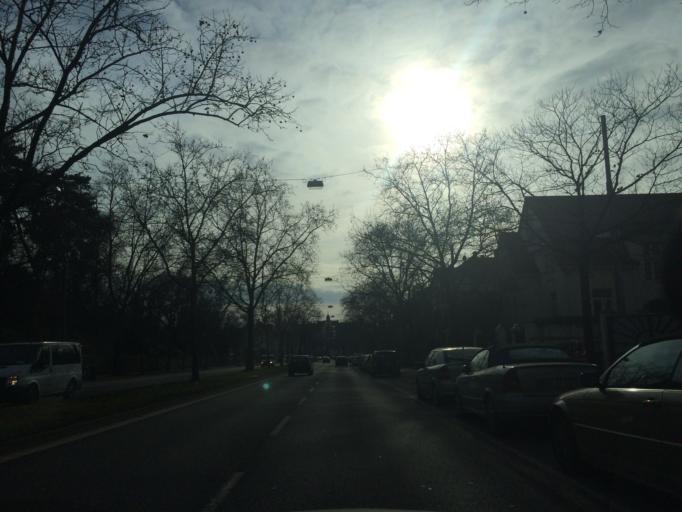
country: DE
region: Hesse
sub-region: Regierungsbezirk Darmstadt
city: Wiesbaden
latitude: 50.0508
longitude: 8.2418
